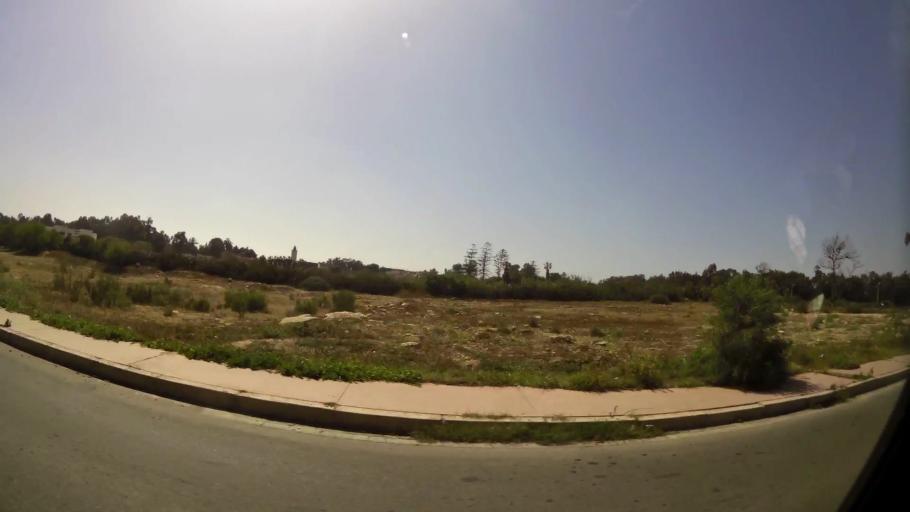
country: MA
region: Souss-Massa-Draa
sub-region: Inezgane-Ait Mellou
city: Inezgane
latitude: 30.3723
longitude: -9.5580
